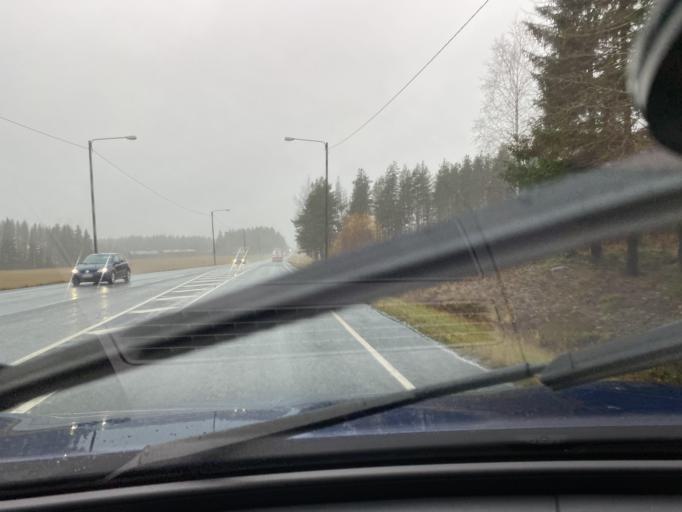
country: FI
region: Haeme
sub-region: Forssa
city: Jokioinen
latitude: 60.7883
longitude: 23.4868
